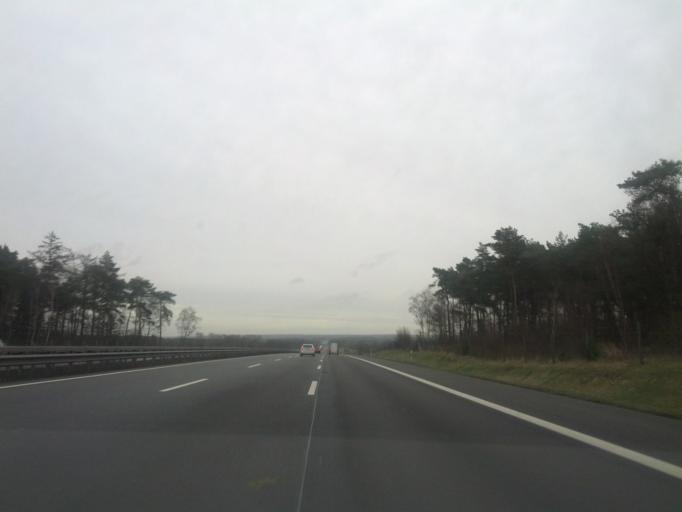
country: DE
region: Lower Saxony
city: Heidenau
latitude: 53.3484
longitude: 9.6738
